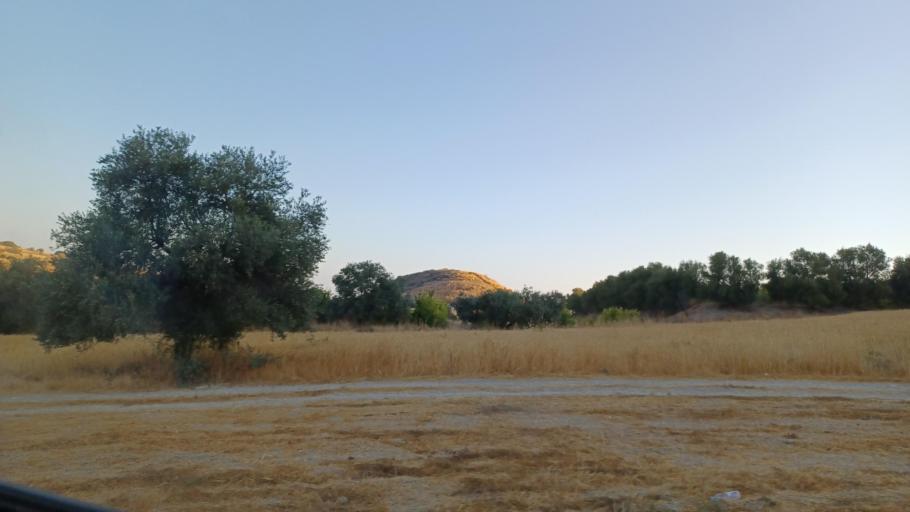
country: CY
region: Pafos
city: Polis
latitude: 35.0001
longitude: 32.4272
